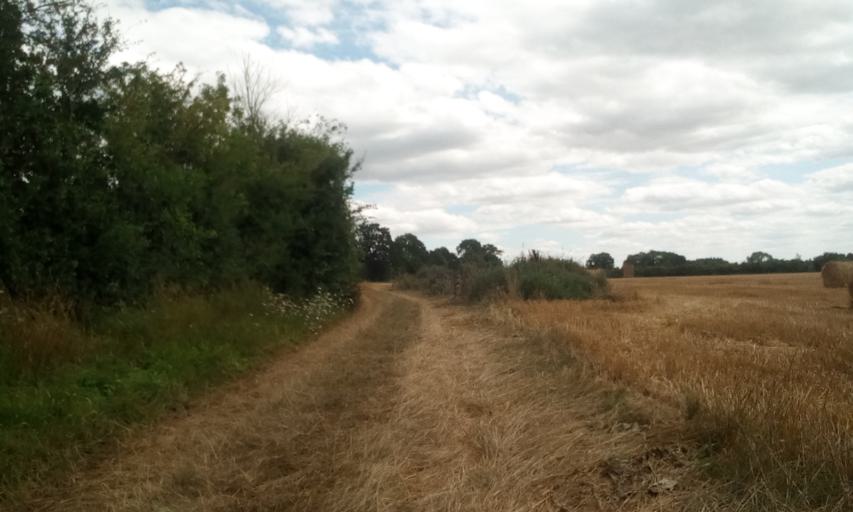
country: FR
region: Lower Normandy
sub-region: Departement du Calvados
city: Troarn
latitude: 49.1671
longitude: -0.1918
